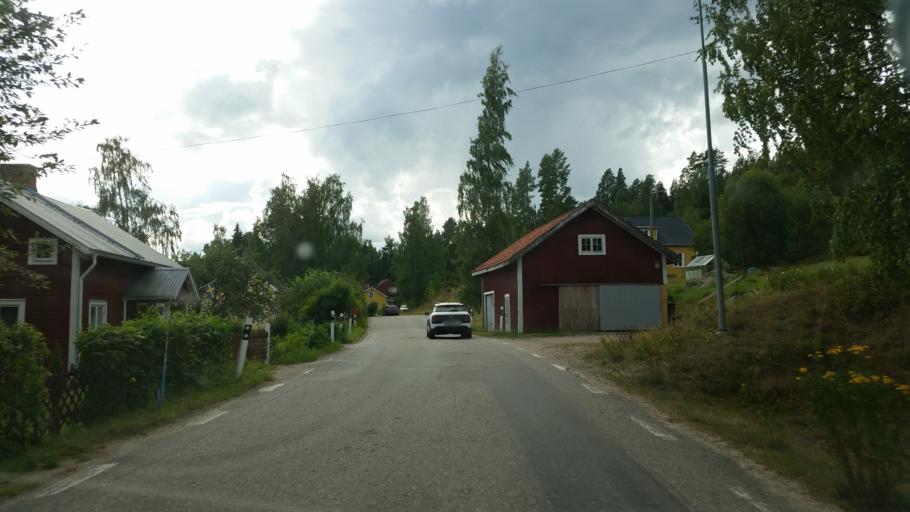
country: SE
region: Gaevleborg
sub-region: Hudiksvalls Kommun
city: Delsbo
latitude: 61.9207
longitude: 16.6098
